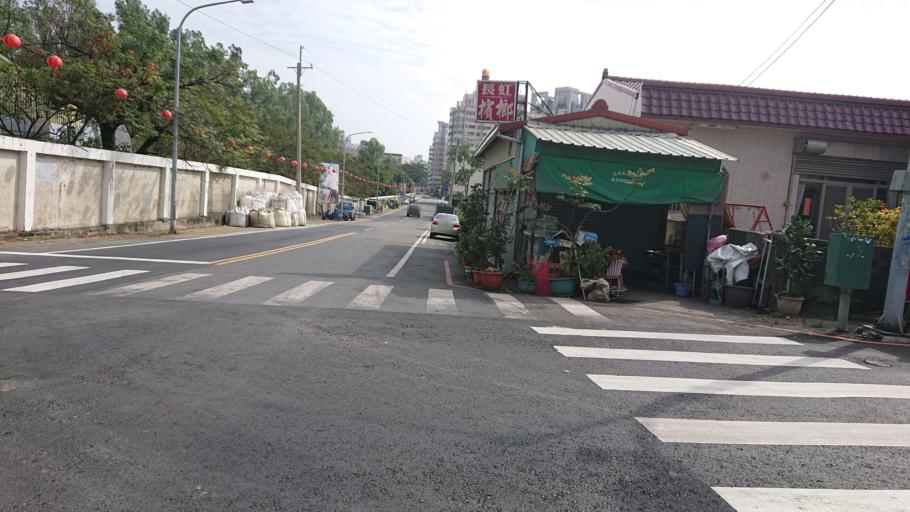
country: TW
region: Taiwan
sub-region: Tainan
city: Tainan
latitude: 23.0202
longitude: 120.2549
